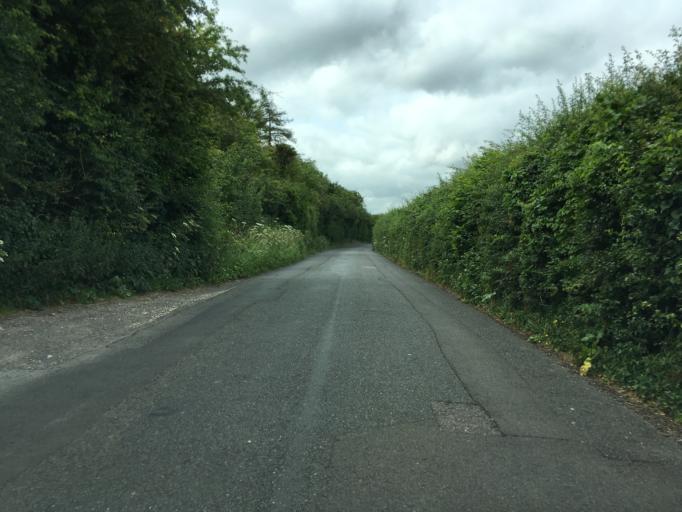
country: GB
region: England
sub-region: Oxfordshire
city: Shipton under Wychwood
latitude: 51.8741
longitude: -1.6669
